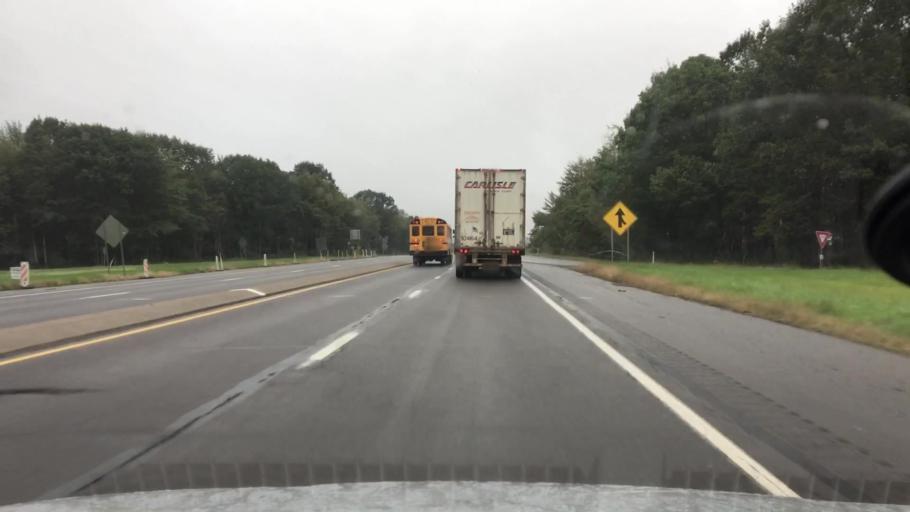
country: US
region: Pennsylvania
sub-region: Monroe County
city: Mount Pocono
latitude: 41.1097
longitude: -75.3885
